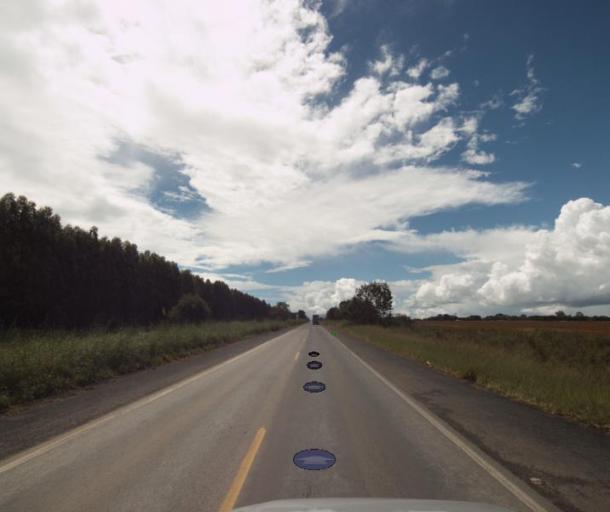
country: BR
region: Goias
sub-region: Uruacu
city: Uruacu
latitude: -14.1739
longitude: -49.1250
